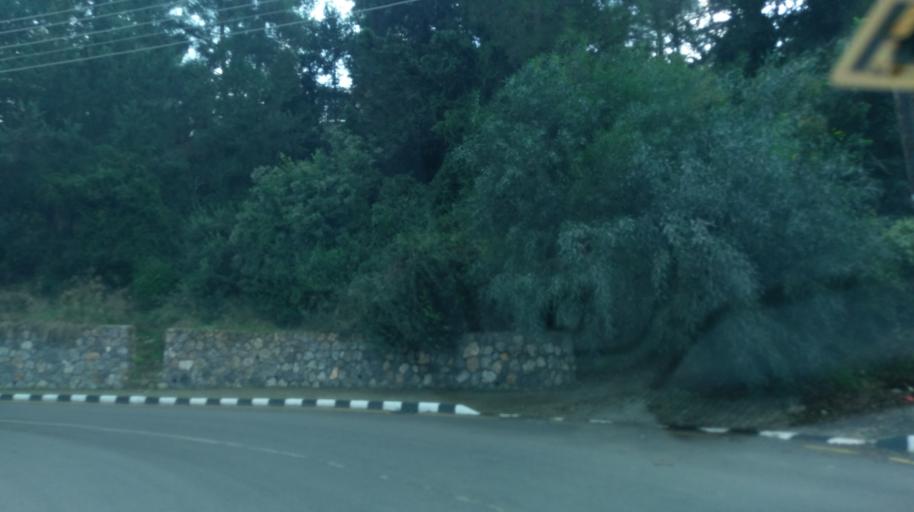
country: CY
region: Keryneia
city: Kyrenia
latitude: 35.3216
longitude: 33.3948
